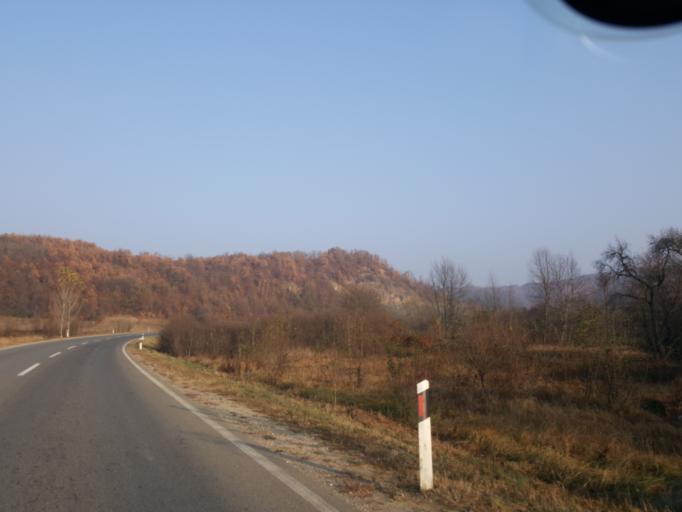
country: RS
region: Central Serbia
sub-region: Jablanicki Okrug
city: Vlasotince
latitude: 42.8996
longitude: 22.0450
